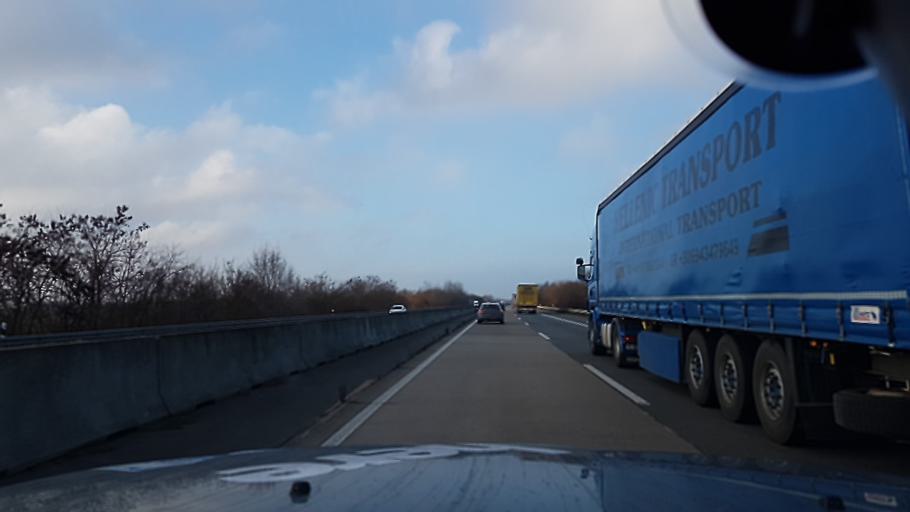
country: DE
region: North Rhine-Westphalia
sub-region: Regierungsbezirk Munster
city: Dreierwalde
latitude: 52.3008
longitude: 7.4978
